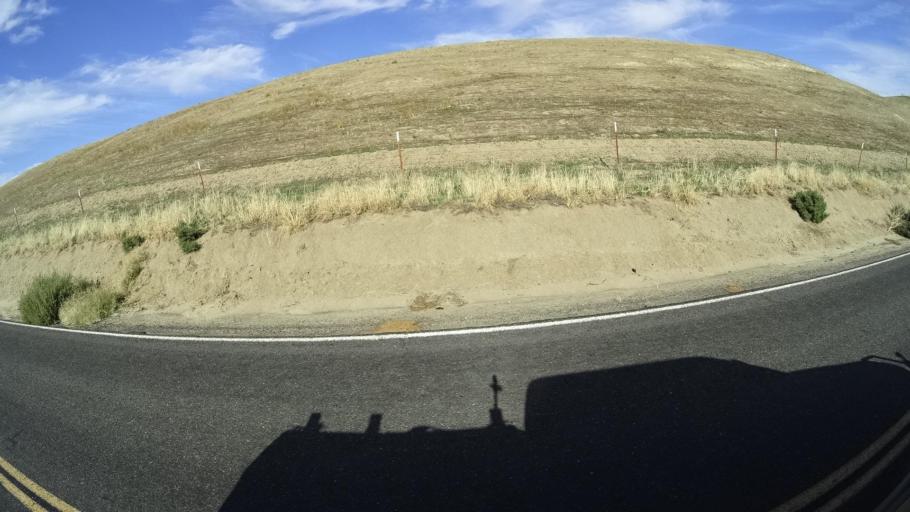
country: US
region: California
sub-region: Kern County
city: Oildale
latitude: 35.6104
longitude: -118.8916
